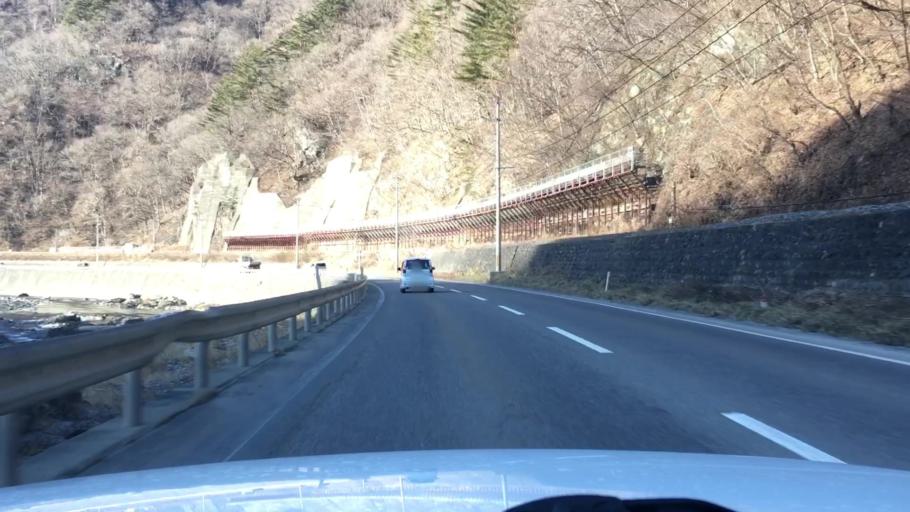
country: JP
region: Iwate
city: Miyako
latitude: 39.6099
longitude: 141.7780
